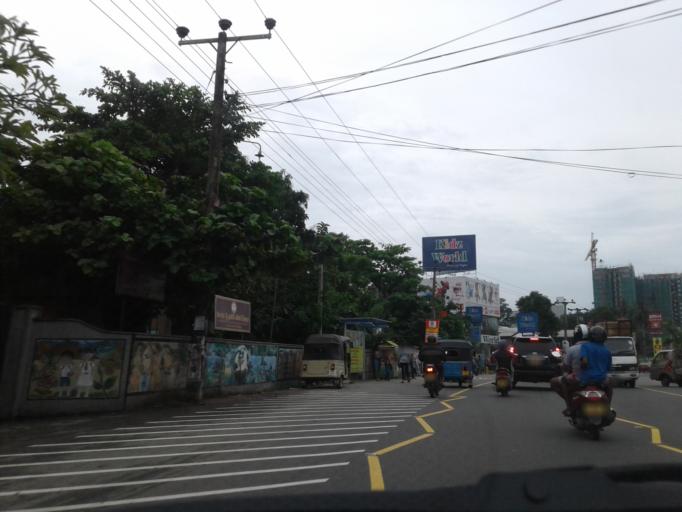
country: LK
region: Western
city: Battaramulla South
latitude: 6.9083
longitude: 79.9365
